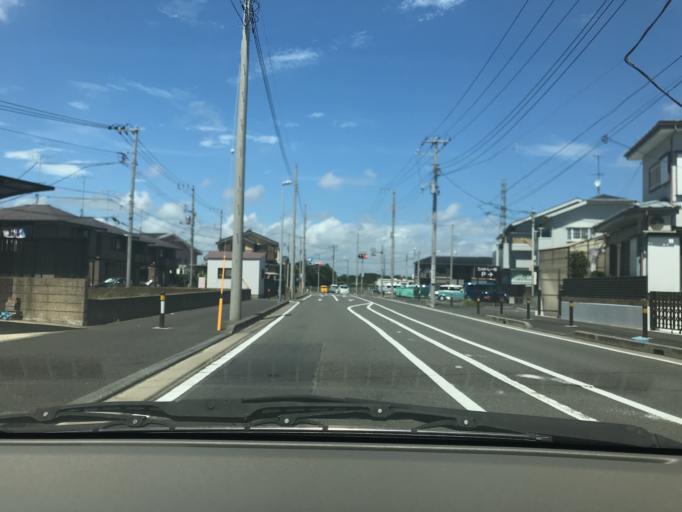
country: JP
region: Kanagawa
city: Fujisawa
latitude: 35.3655
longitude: 139.4607
